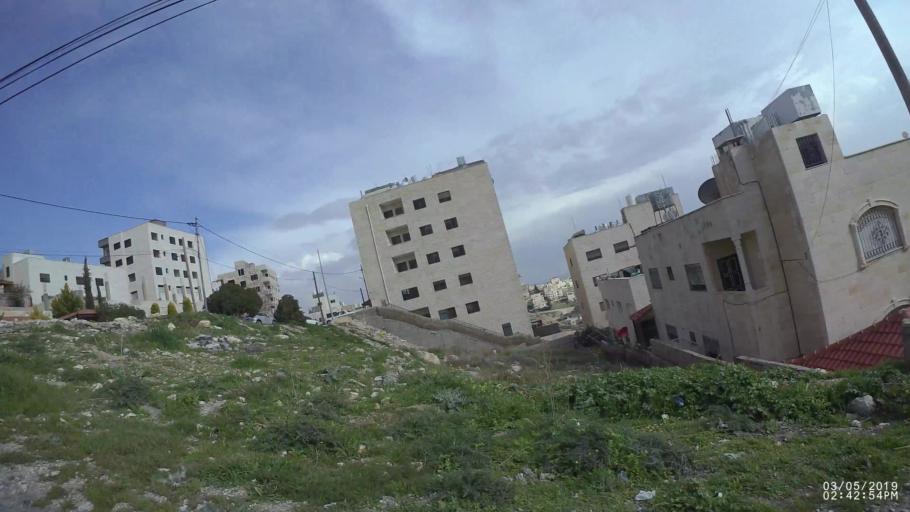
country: JO
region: Amman
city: Amman
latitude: 32.0120
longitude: 35.9415
